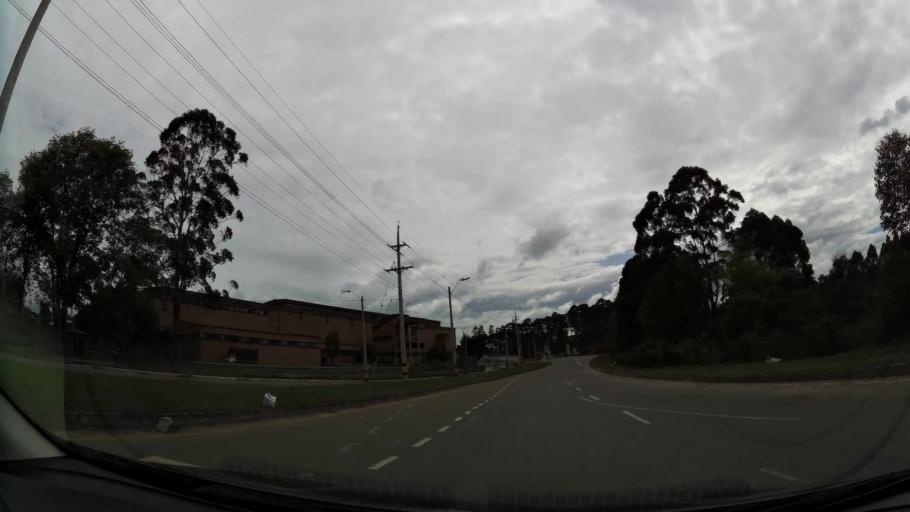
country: CO
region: Antioquia
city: Rionegro
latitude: 6.1732
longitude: -75.3632
